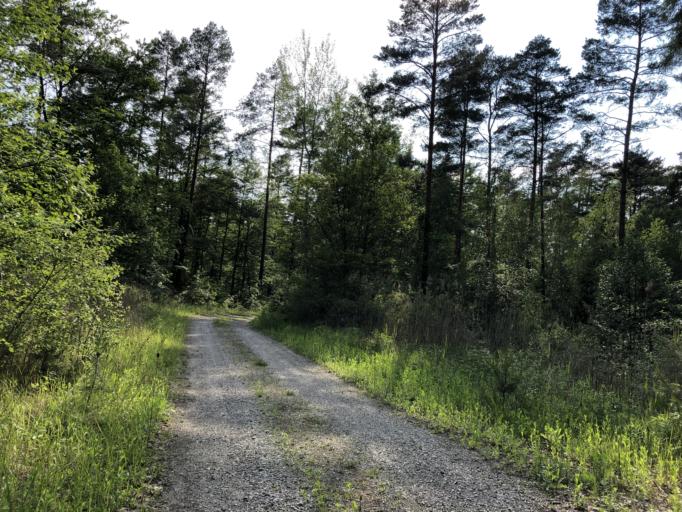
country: DE
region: Bavaria
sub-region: Upper Franconia
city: Memmelsdorf
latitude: 49.9105
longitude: 10.9529
